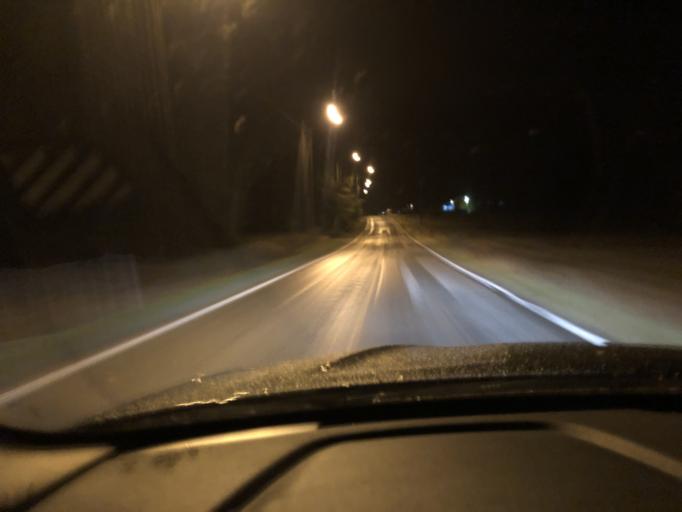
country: FI
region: Pirkanmaa
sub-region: Etelae-Pirkanmaa
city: Akaa
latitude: 61.1441
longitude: 23.8524
